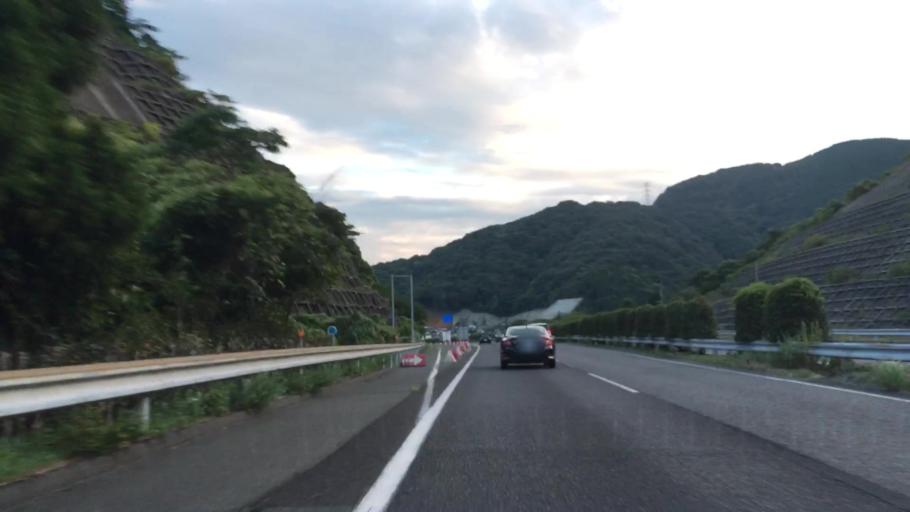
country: JP
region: Yamaguchi
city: Shimonoseki
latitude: 33.8920
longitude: 130.9710
